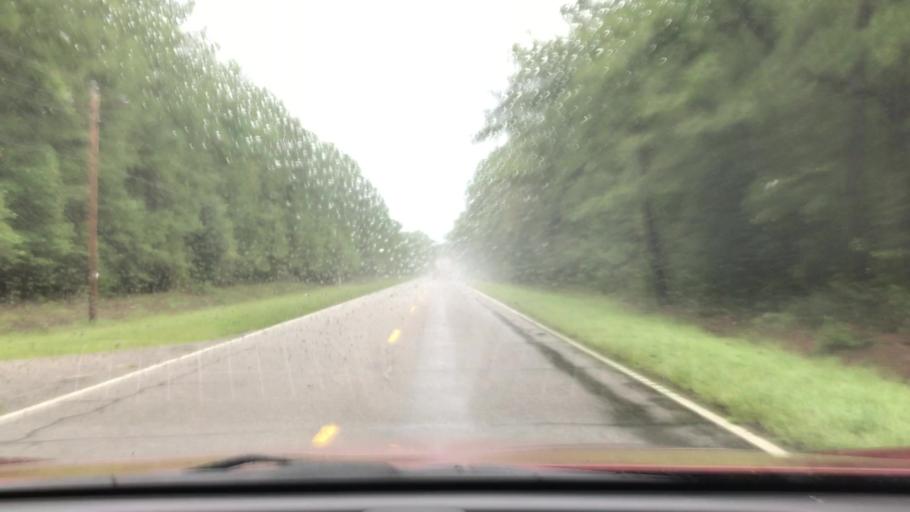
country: US
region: South Carolina
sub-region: Georgetown County
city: Georgetown
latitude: 33.4922
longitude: -79.2638
